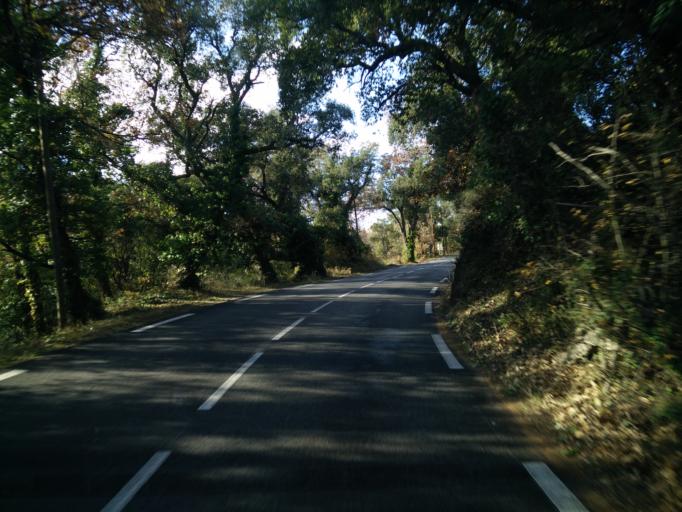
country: FR
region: Provence-Alpes-Cote d'Azur
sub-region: Departement du Var
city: La Garde-Freinet
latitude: 43.3263
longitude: 6.4735
